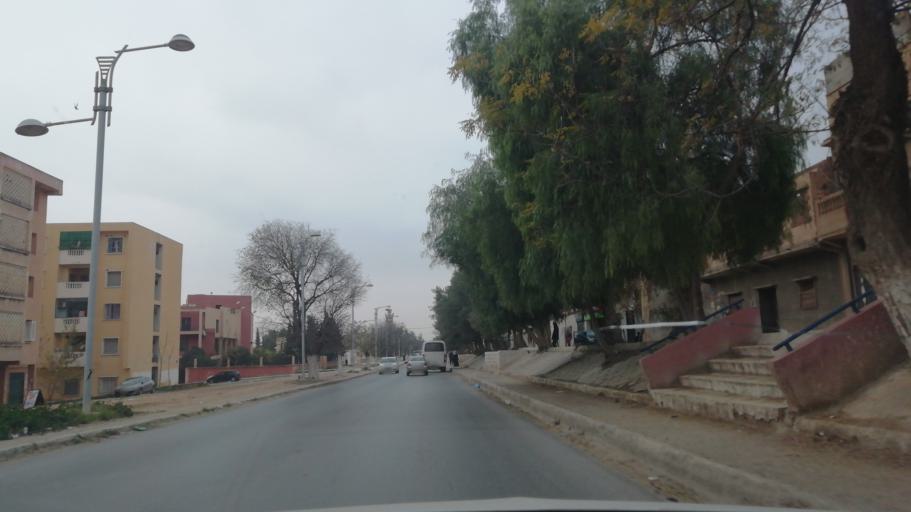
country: DZ
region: Sidi Bel Abbes
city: Sfizef
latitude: 35.2393
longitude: -0.2335
